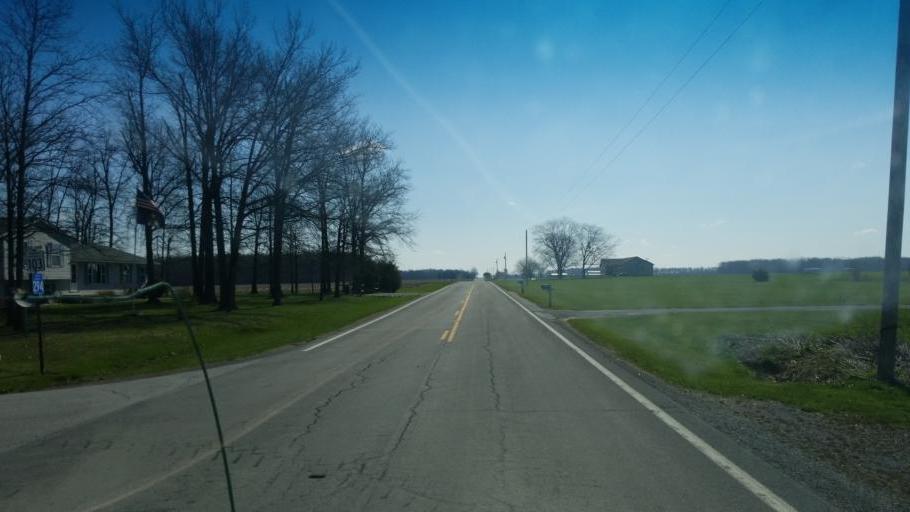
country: US
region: Ohio
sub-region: Wyandot County
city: Upper Sandusky
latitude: 40.7375
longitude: -83.3542
